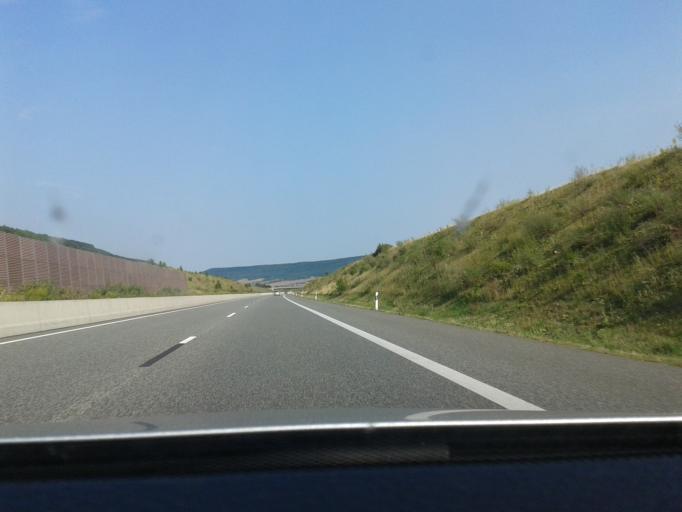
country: DE
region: Thuringia
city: Sollstedt
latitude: 51.4229
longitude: 10.5309
